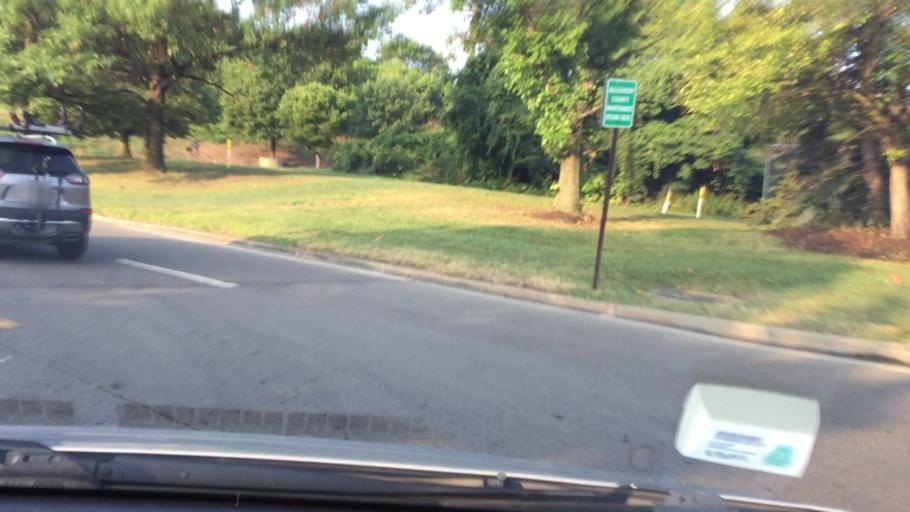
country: US
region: Pennsylvania
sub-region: Butler County
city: Cranberry Township
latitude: 40.6670
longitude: -80.1021
